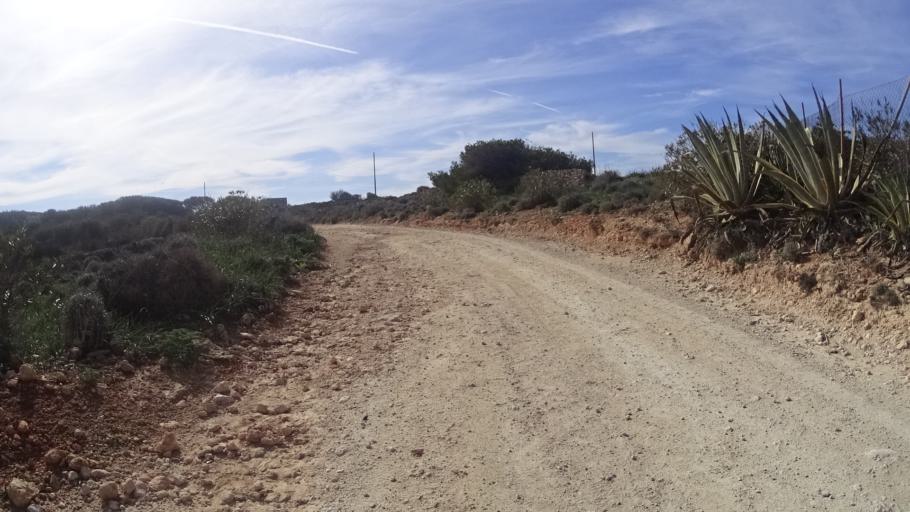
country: MT
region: Il-Qala
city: Qala
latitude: 36.0154
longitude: 14.3279
